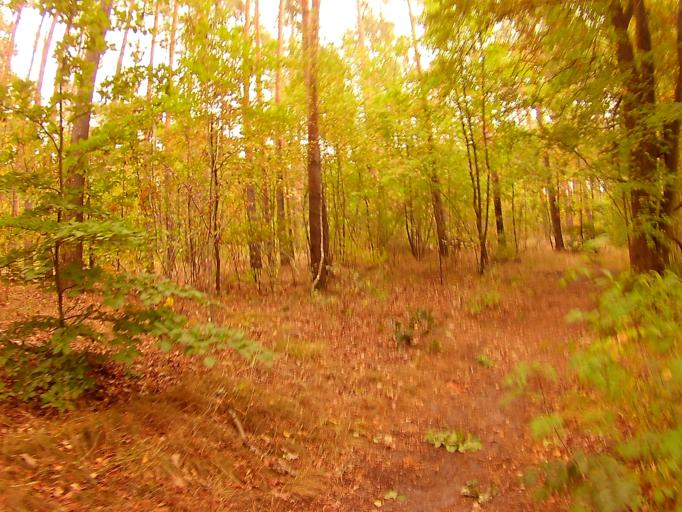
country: DE
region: Berlin
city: Grunau
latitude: 52.4055
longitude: 13.6077
